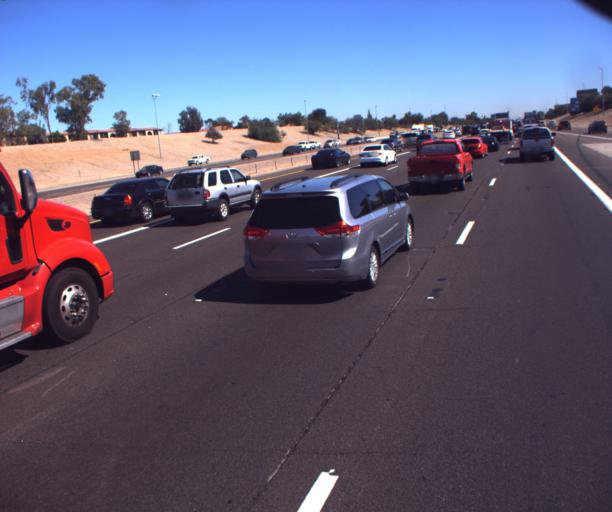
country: US
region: Arizona
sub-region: Maricopa County
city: Glendale
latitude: 33.4627
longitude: -112.1832
